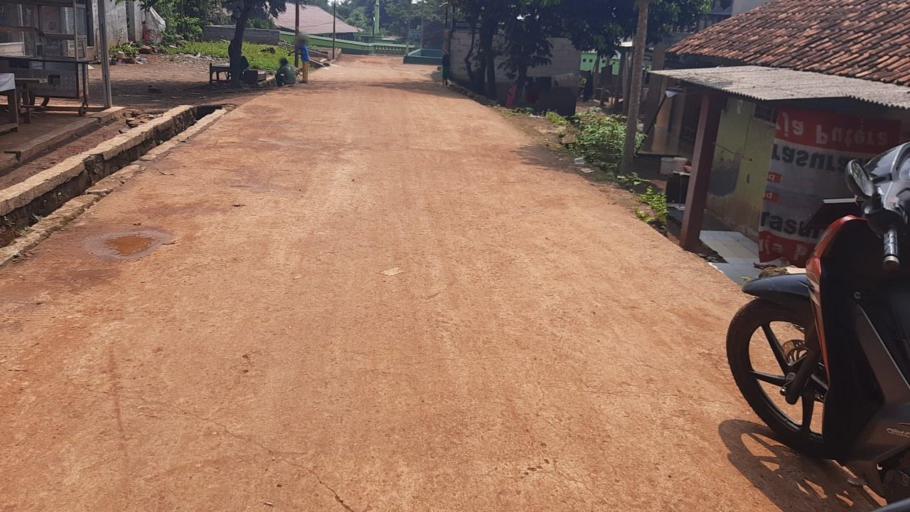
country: ID
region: West Java
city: Cileungsir
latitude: -6.4202
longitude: 106.9138
